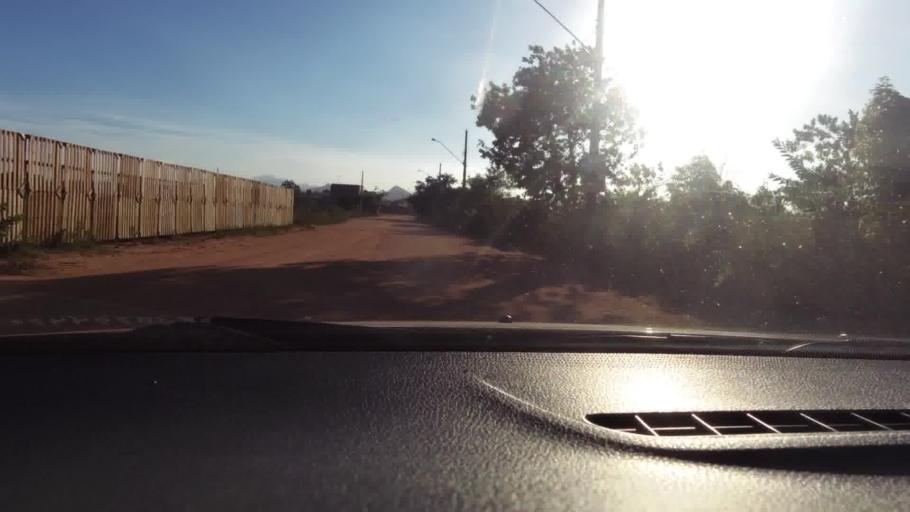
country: BR
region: Espirito Santo
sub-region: Guarapari
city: Guarapari
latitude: -20.5551
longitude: -40.4076
